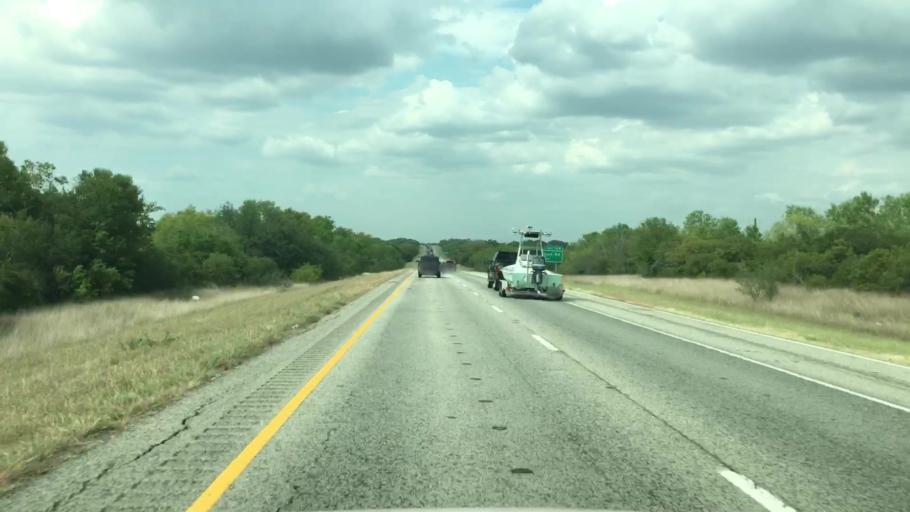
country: US
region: Texas
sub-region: Atascosa County
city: Pleasanton
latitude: 28.9268
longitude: -98.4350
